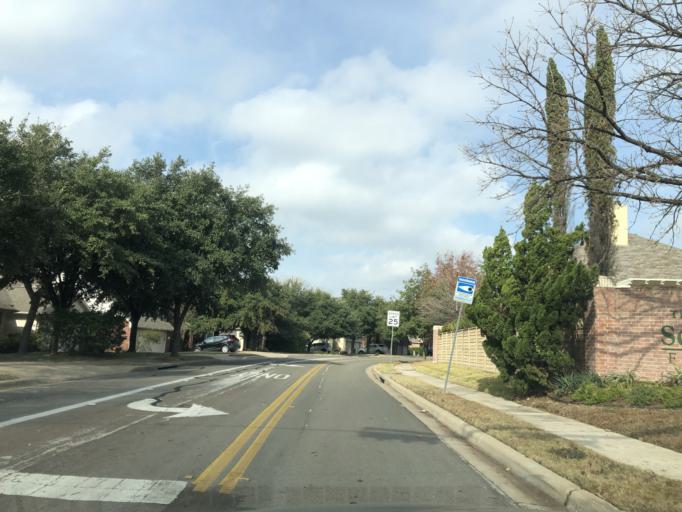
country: US
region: Texas
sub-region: Travis County
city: Wells Branch
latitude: 30.4224
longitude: -97.6824
